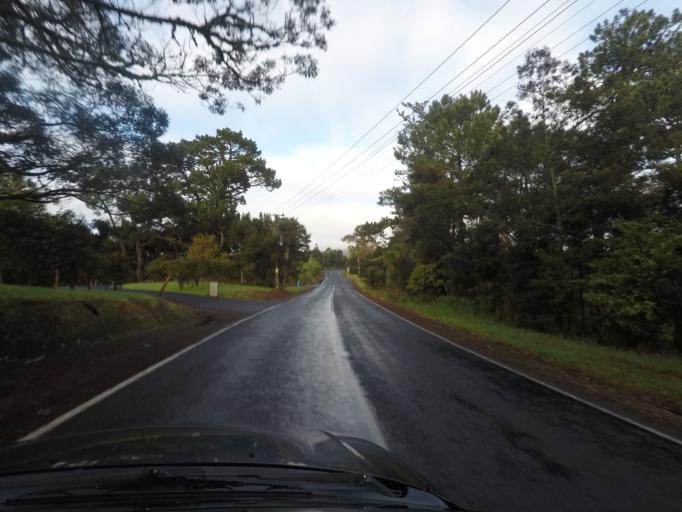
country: NZ
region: Auckland
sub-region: Auckland
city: Waitakere
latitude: -36.9102
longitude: 174.6091
